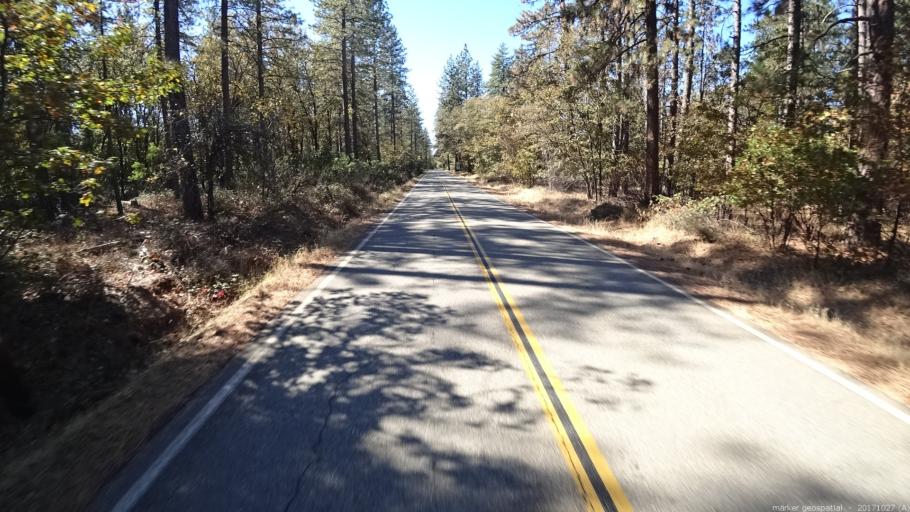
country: US
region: California
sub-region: Shasta County
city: Bella Vista
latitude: 40.6895
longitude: -122.0195
